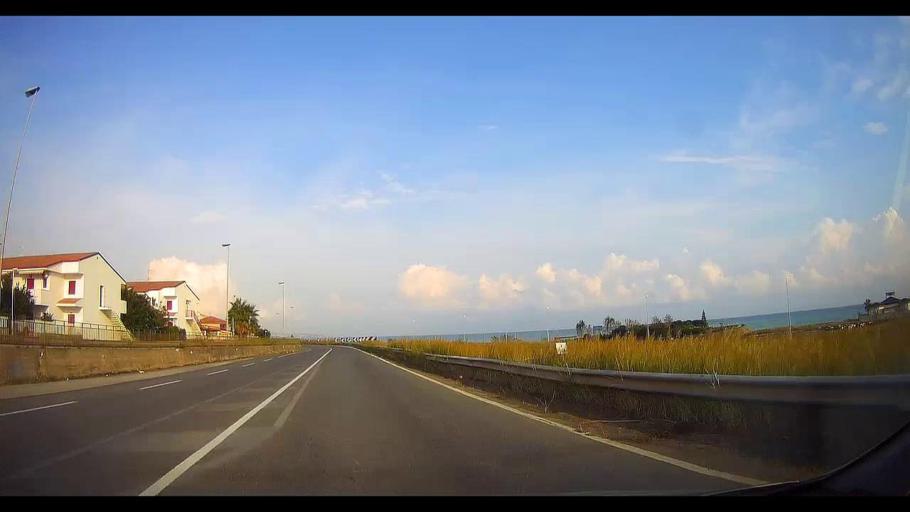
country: IT
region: Calabria
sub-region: Provincia di Cosenza
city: Cariati
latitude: 39.5268
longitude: 16.8885
